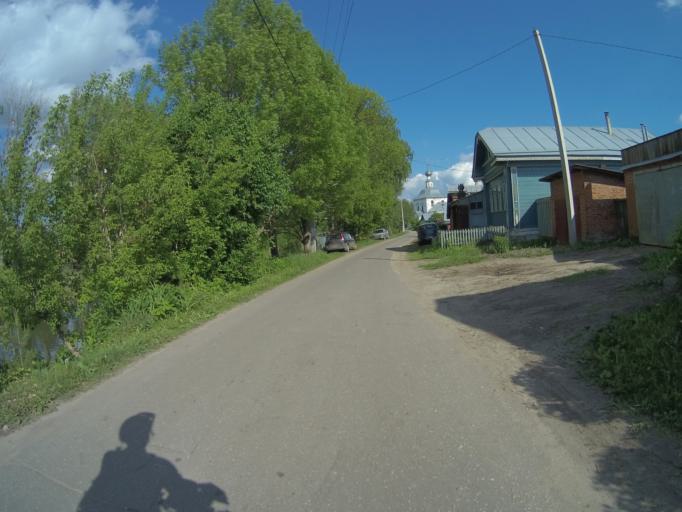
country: RU
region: Vladimir
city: Suzdal'
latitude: 56.4213
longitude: 40.4398
